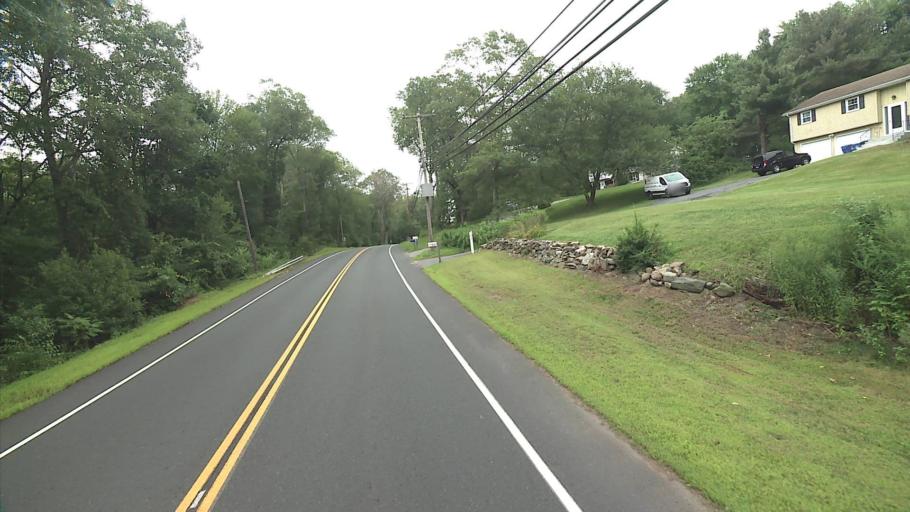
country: US
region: Connecticut
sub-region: Tolland County
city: Tolland
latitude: 41.8774
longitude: -72.3909
